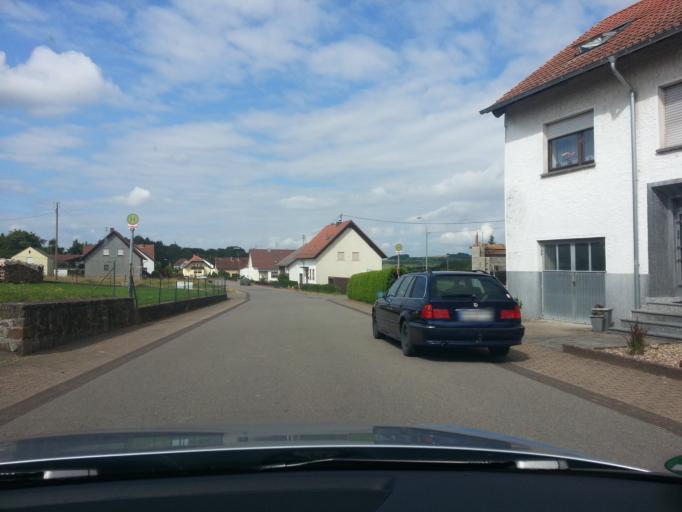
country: DE
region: Saarland
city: Weiten
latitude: 49.5282
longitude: 6.5308
